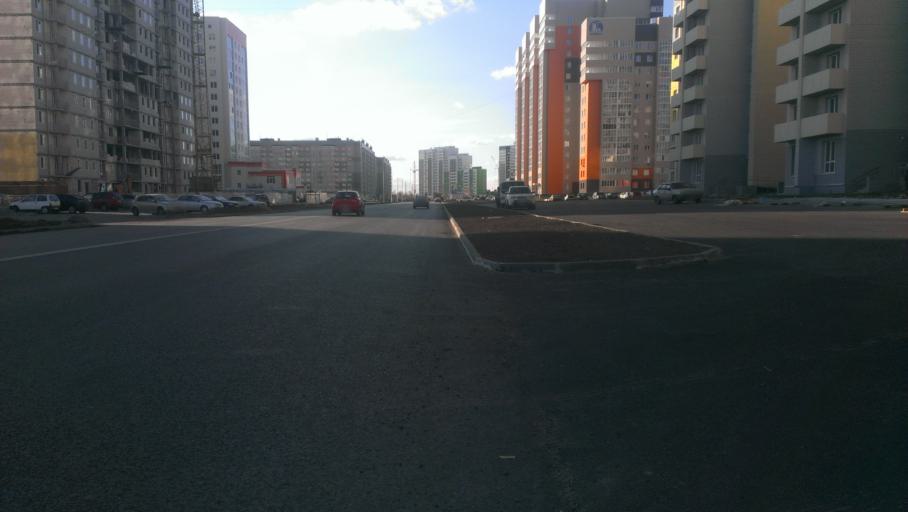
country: RU
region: Altai Krai
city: Novosilikatnyy
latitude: 53.3372
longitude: 83.6591
